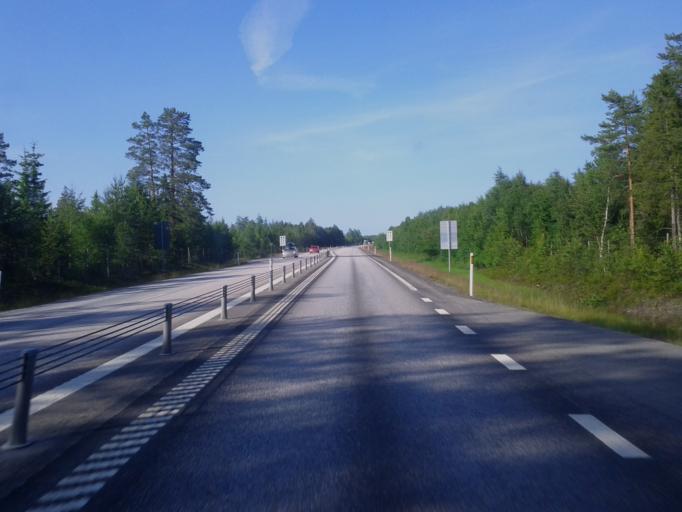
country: SE
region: Vaesterbotten
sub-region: Umea Kommun
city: Saevar
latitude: 63.9477
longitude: 20.6601
